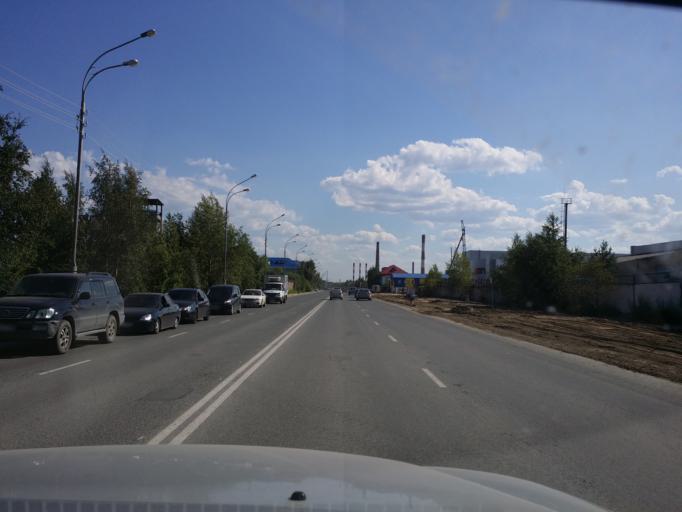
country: RU
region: Khanty-Mansiyskiy Avtonomnyy Okrug
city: Nizhnevartovsk
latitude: 60.9441
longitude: 76.5482
